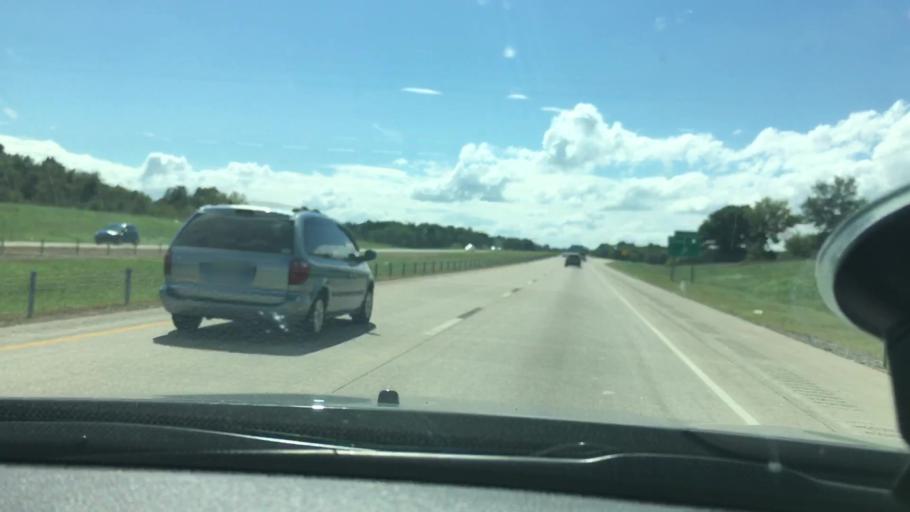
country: US
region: Oklahoma
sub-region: Muskogee County
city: Warner
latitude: 35.4852
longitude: -95.1965
